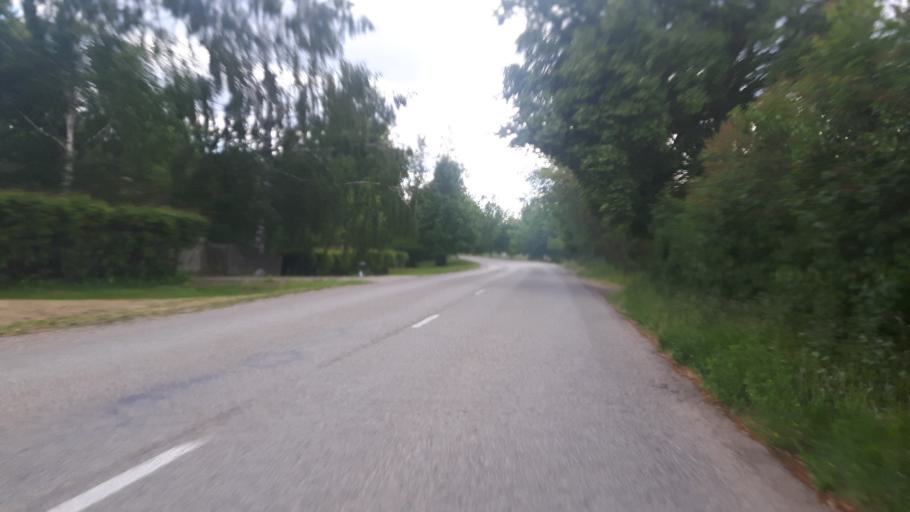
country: LV
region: Engure
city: Smarde
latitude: 57.0340
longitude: 23.3655
